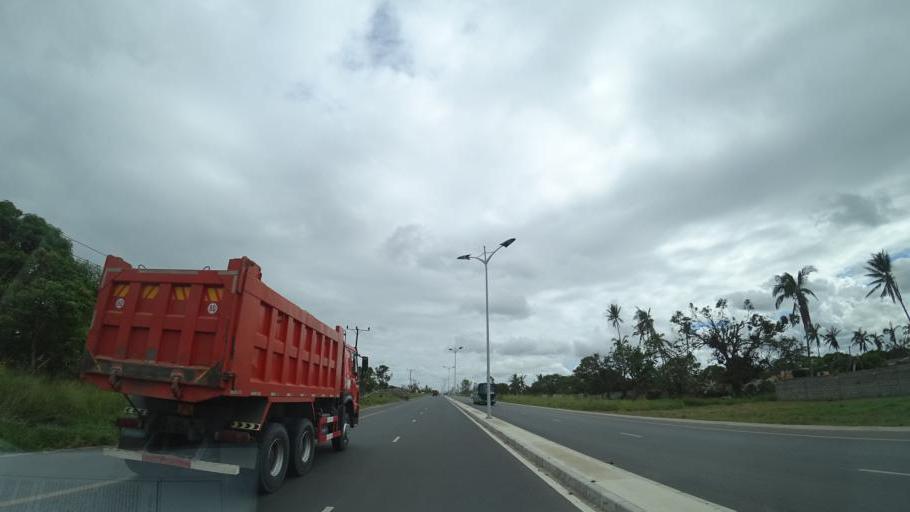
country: MZ
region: Sofala
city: Dondo
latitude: -19.7124
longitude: 34.7980
